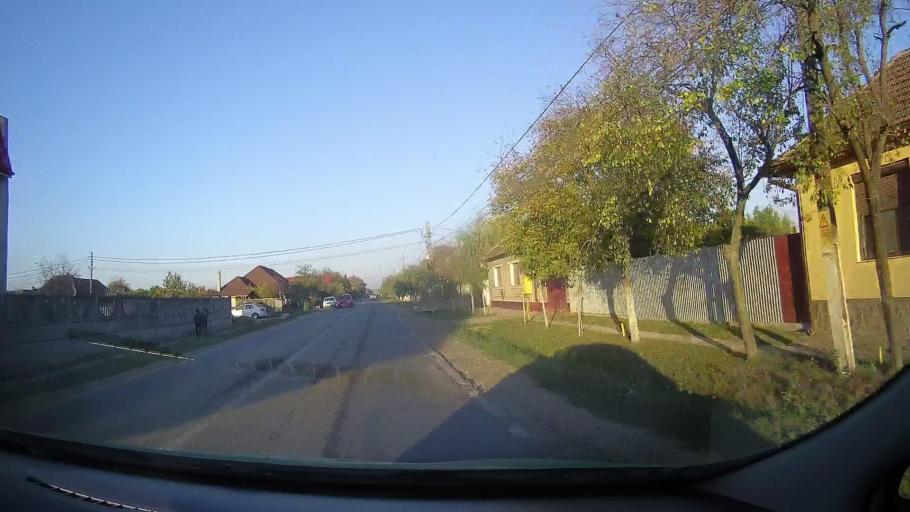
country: RO
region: Bihor
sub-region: Comuna Salard
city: Salard
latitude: 47.2152
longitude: 22.0291
